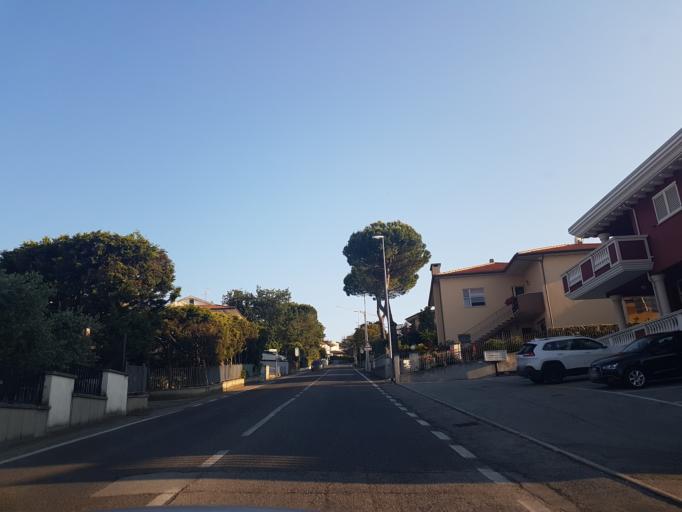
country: SM
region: Domagnano
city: Domagnano
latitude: 43.9594
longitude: 12.4689
